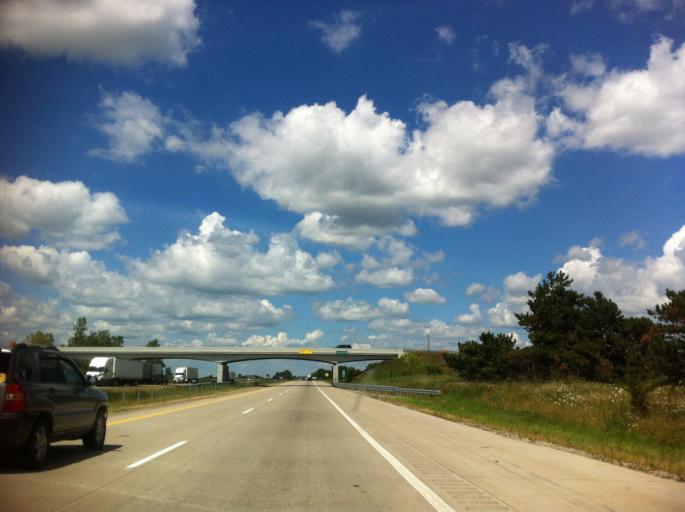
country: US
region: Ohio
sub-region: Lucas County
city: Sylvania
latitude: 41.7678
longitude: -83.6948
